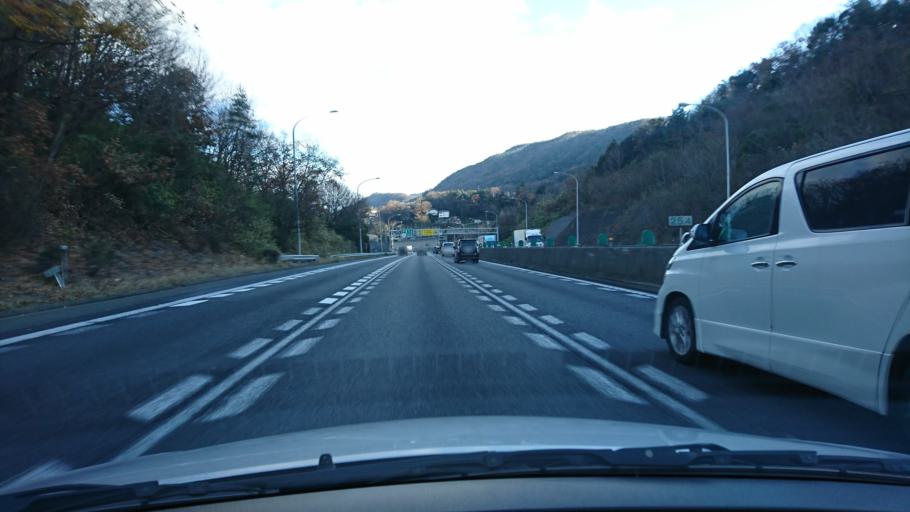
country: JP
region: Hyogo
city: Sandacho
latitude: 34.8327
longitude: 135.2832
